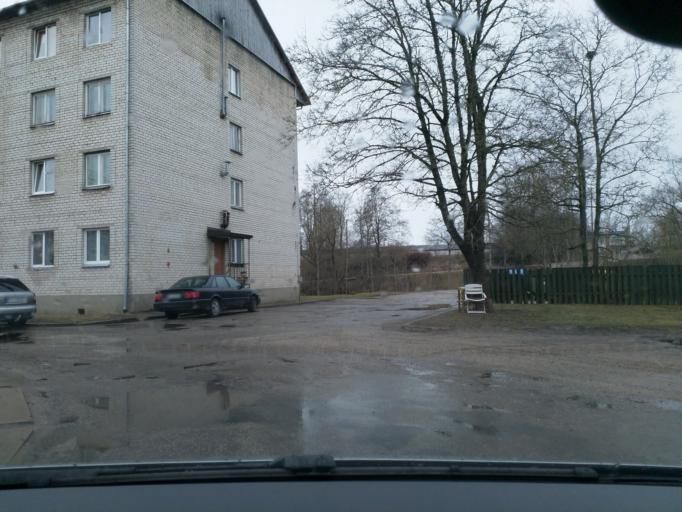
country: LV
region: Kuldigas Rajons
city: Kuldiga
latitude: 56.9800
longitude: 21.9611
